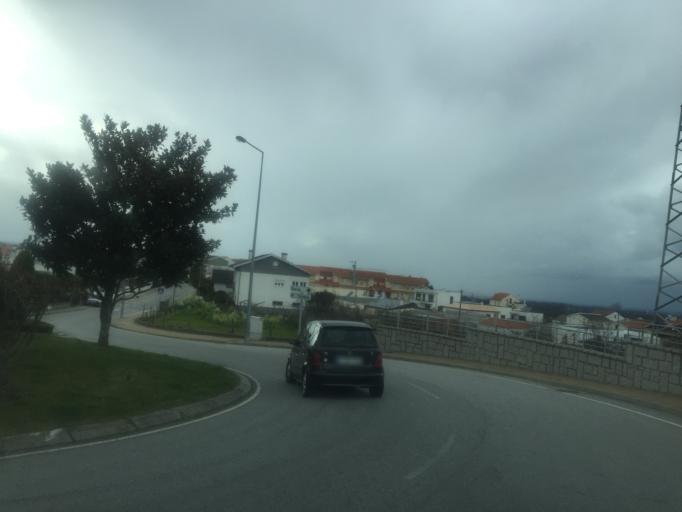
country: PT
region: Guarda
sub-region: Seia
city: Seia
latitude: 40.4043
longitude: -7.7225
